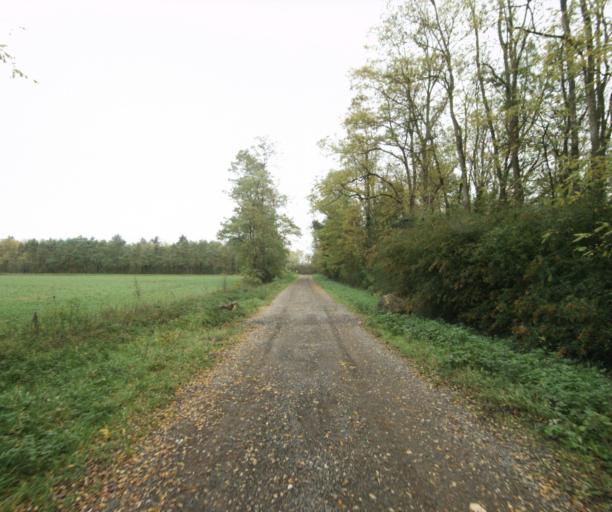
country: FR
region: Rhone-Alpes
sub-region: Departement de l'Ain
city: Pont-de-Vaux
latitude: 46.4615
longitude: 4.8962
